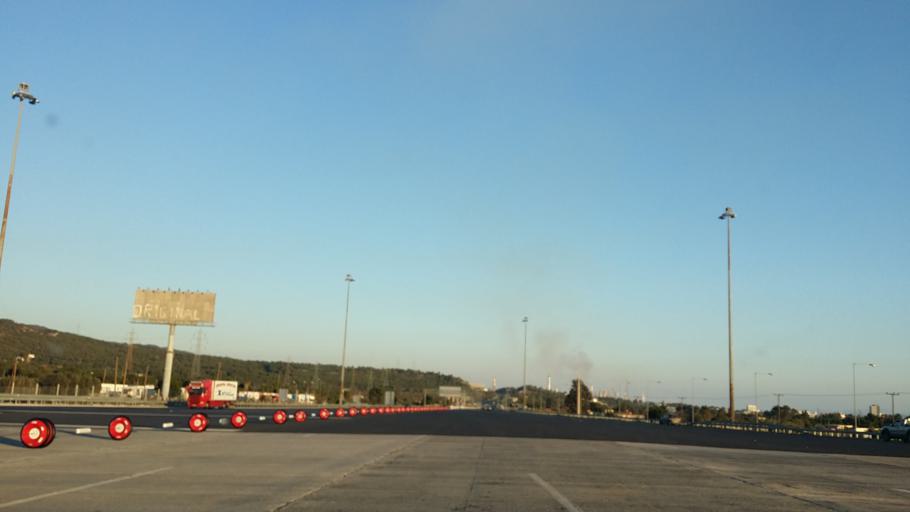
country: GR
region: Peloponnese
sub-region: Nomos Korinthias
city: Isthmia
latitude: 37.9251
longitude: 23.0342
